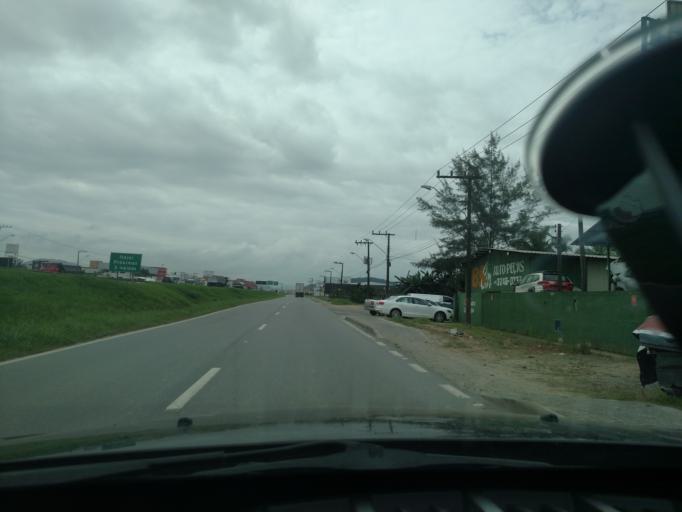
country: BR
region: Santa Catarina
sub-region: Itajai
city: Itajai
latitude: -26.8699
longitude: -48.7302
